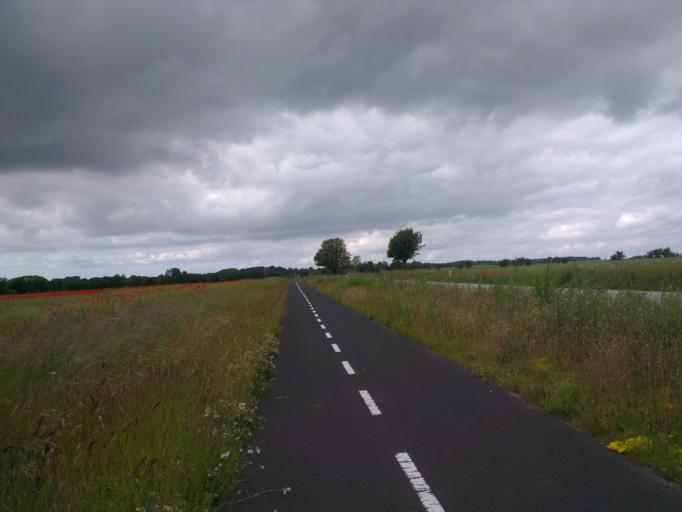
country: DK
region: Capital Region
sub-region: Frederikssund Kommune
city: Skibby
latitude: 55.6928
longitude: 11.9498
